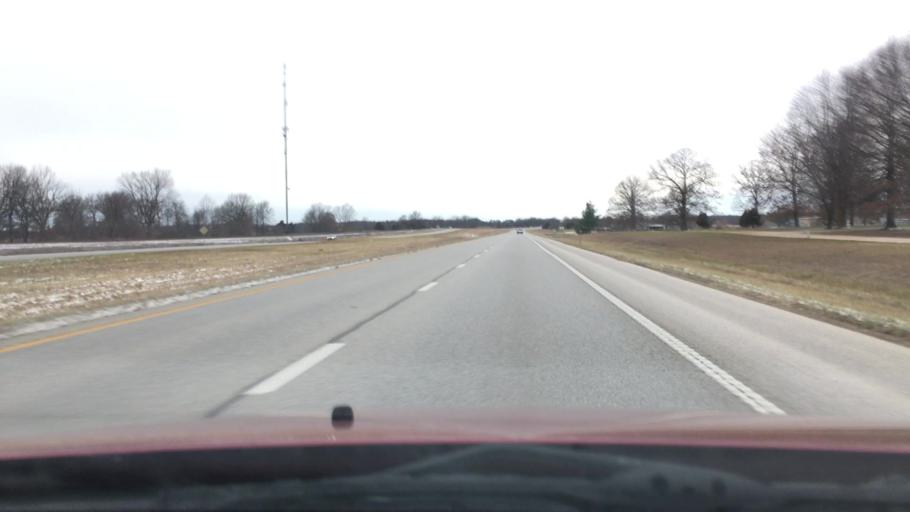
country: US
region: Missouri
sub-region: Webster County
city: Seymour
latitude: 37.1694
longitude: -92.8146
